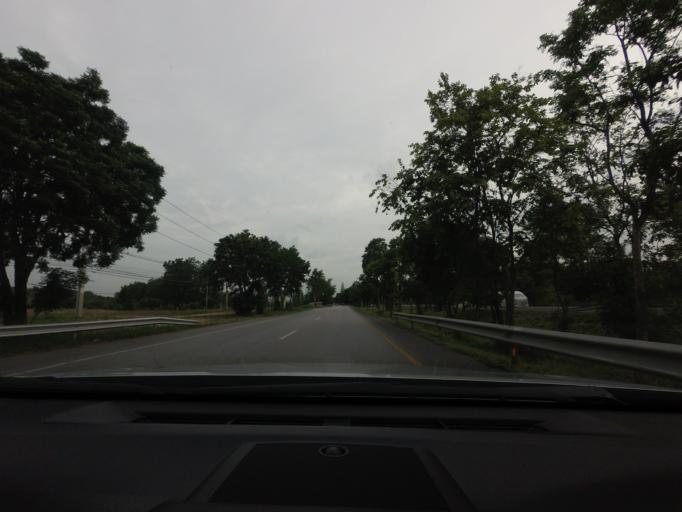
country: TH
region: Prachuap Khiri Khan
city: Hua Hin
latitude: 12.6370
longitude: 99.8602
